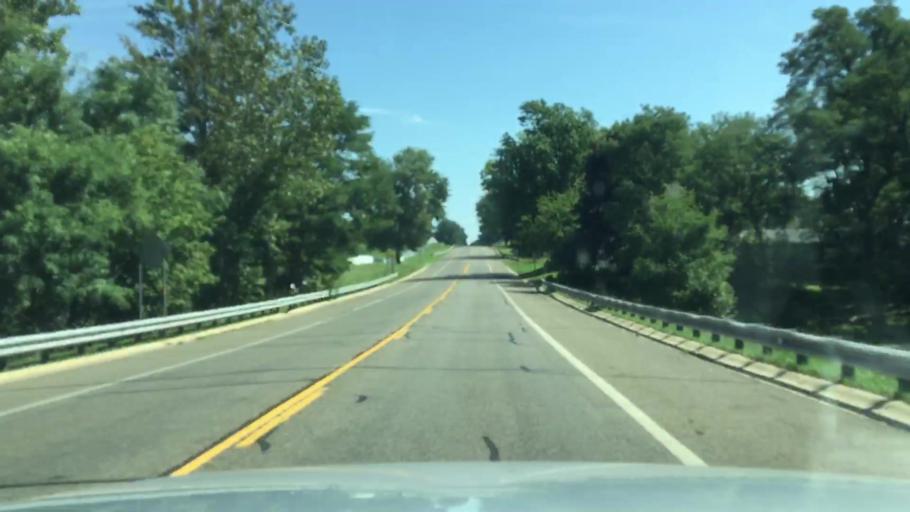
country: US
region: Michigan
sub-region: Jackson County
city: Brooklyn
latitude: 42.0578
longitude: -84.2362
